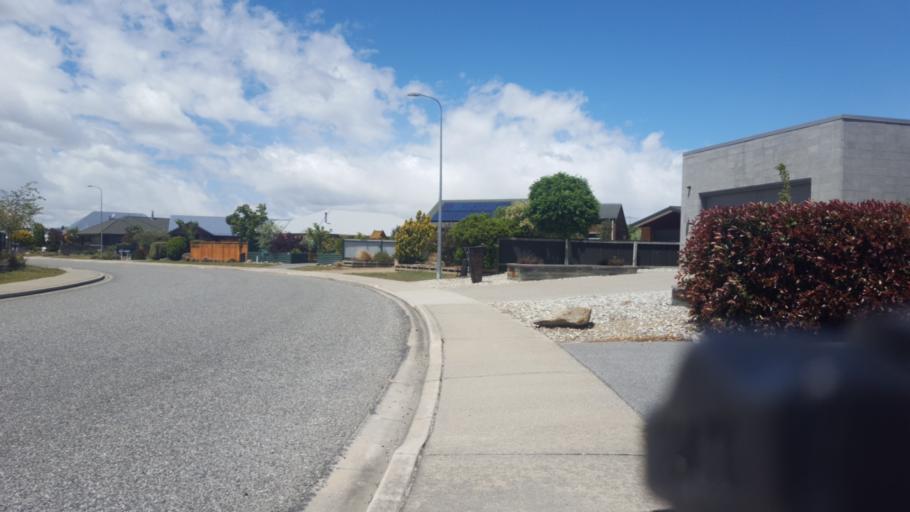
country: NZ
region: Otago
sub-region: Queenstown-Lakes District
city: Wanaka
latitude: -45.1936
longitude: 169.3314
